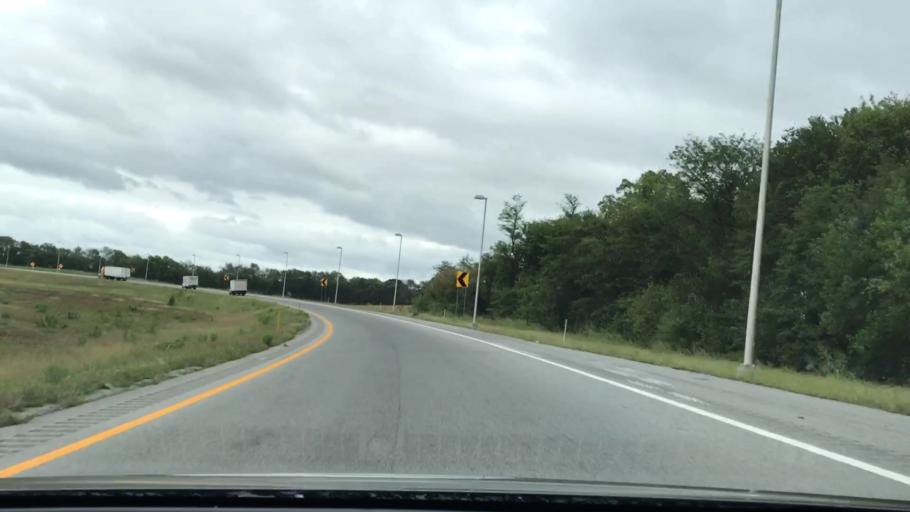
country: US
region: Kentucky
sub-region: Christian County
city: Fort Campbell North
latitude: 36.7392
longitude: -87.5090
